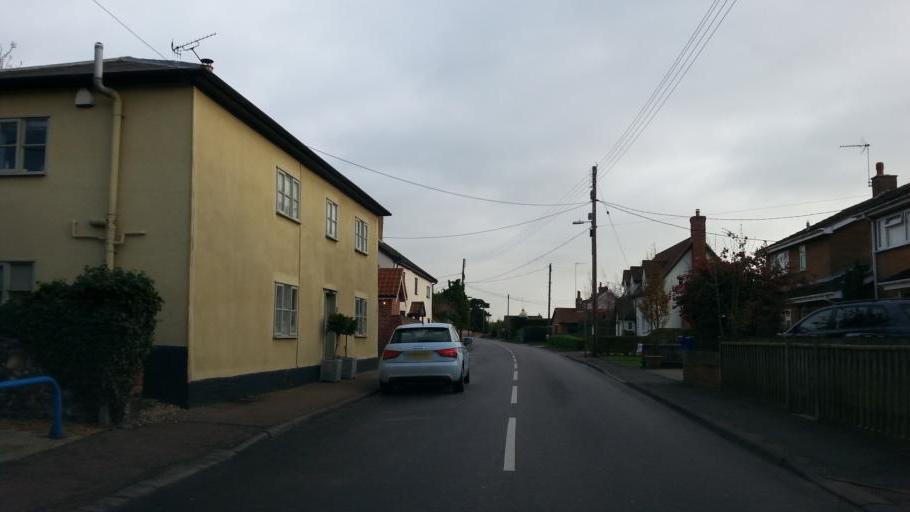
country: GB
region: England
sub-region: Suffolk
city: Ixworth
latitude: 52.2962
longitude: 0.8323
